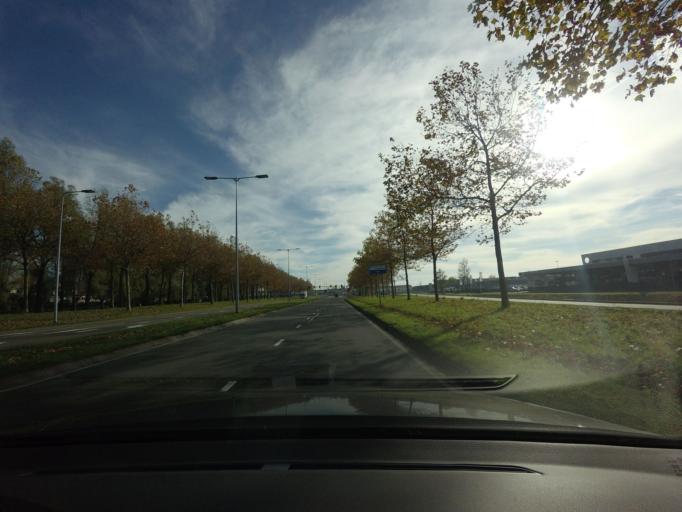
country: NL
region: North Holland
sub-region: Gemeente Haarlemmermeer
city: Hoofddorp
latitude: 52.2929
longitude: 4.6884
